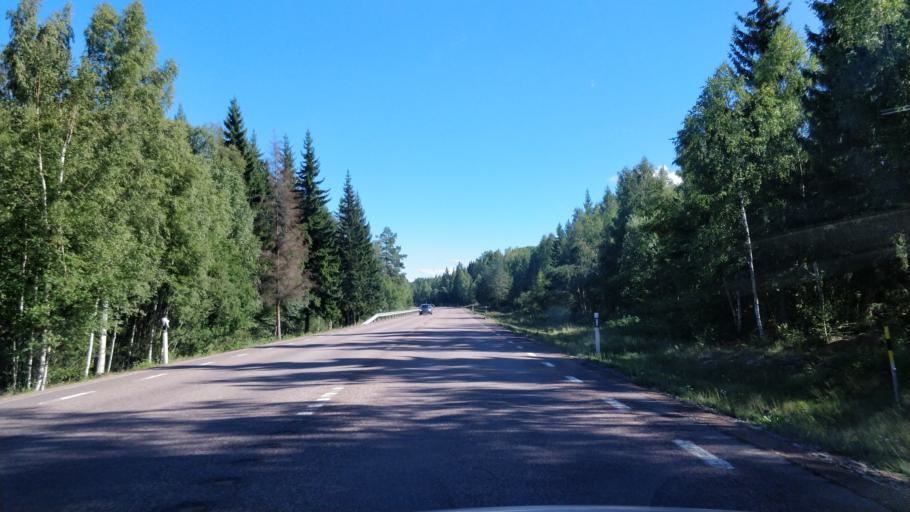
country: SE
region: Dalarna
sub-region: Faluns Kommun
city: Falun
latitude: 60.6454
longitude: 15.5710
